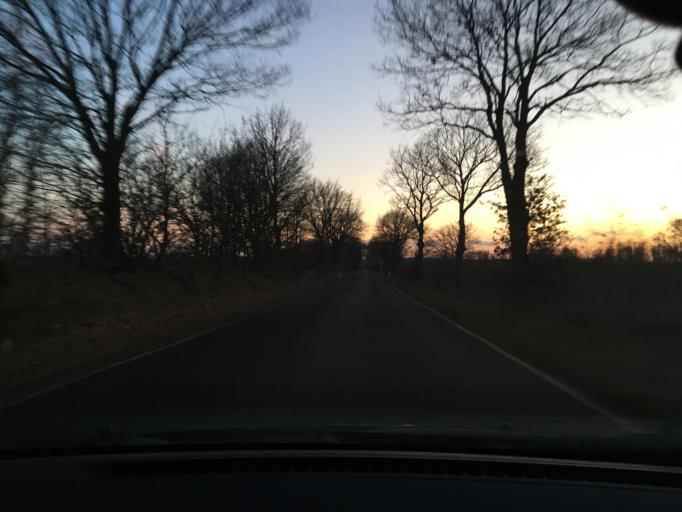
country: DE
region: Schleswig-Holstein
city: Fitzen
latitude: 53.4908
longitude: 10.6443
